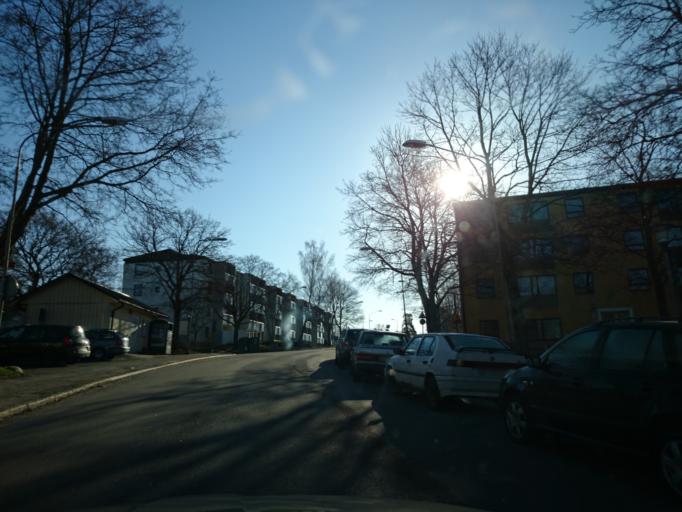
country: SE
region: Stockholm
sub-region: Stockholms Kommun
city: Arsta
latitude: 59.2391
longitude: 18.0949
